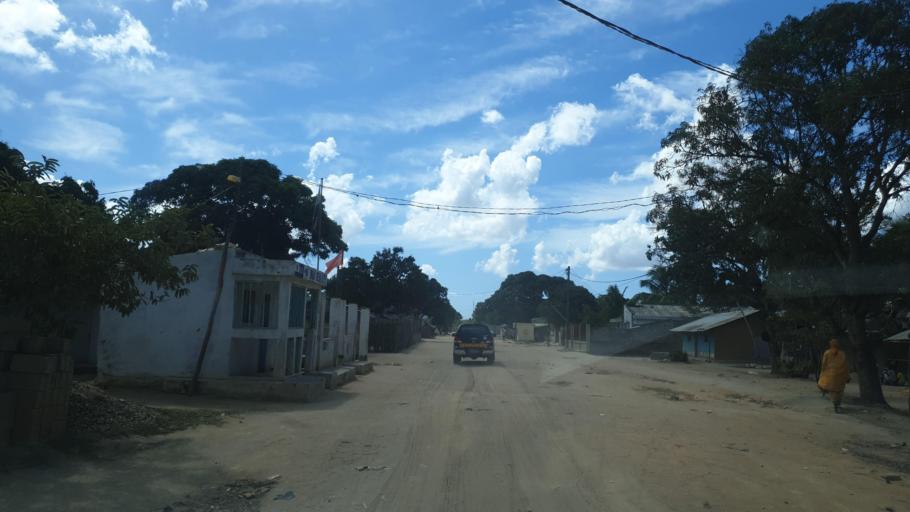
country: MZ
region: Nampula
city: Nacala
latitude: -14.5696
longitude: 40.6950
